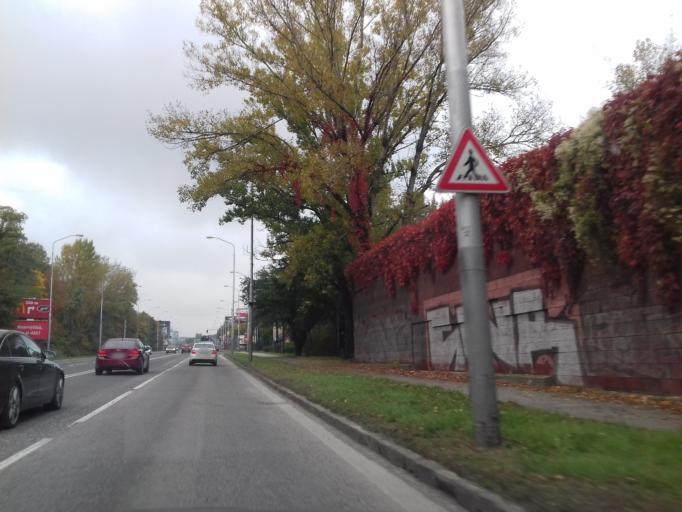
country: SK
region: Bratislavsky
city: Bratislava
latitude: 48.1723
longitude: 17.0703
